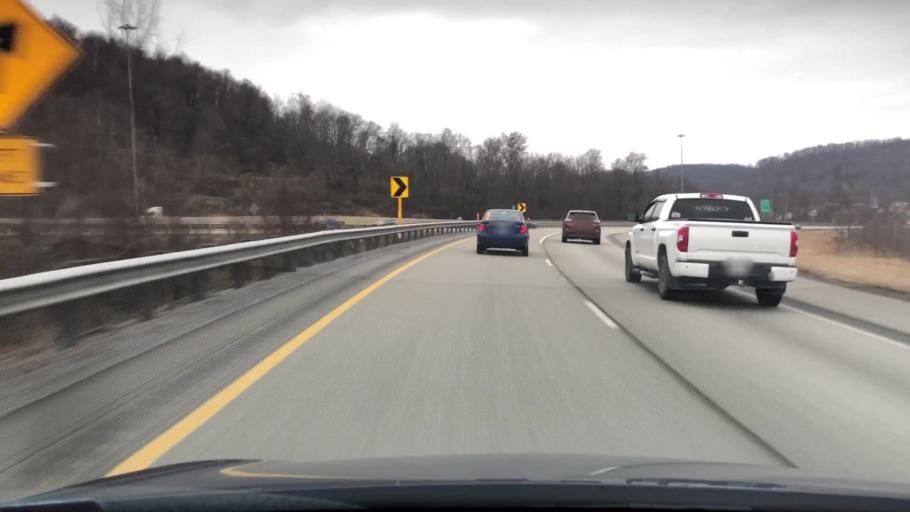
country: US
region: West Virginia
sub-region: Monongalia County
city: Morgantown
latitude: 39.5802
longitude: -79.9764
